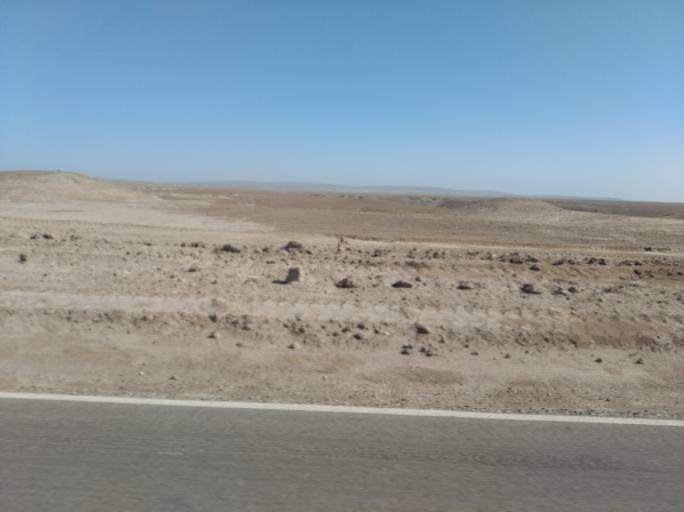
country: CL
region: Atacama
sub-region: Provincia de Copiapo
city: Copiapo
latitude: -27.3174
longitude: -70.8332
